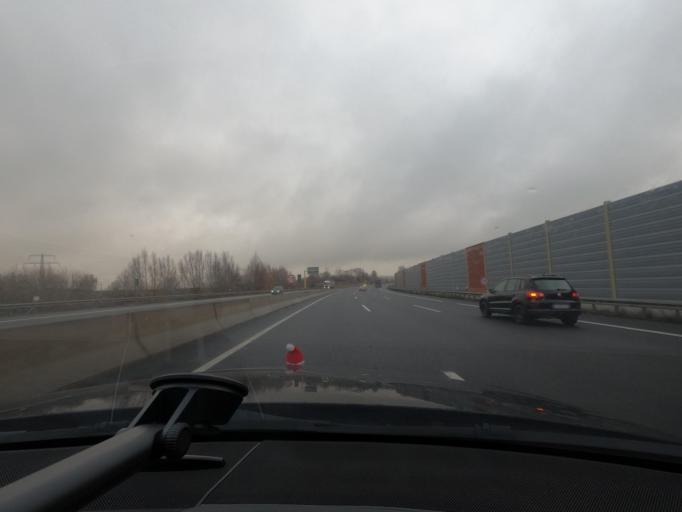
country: DE
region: Lower Saxony
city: Bovenden
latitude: 51.5647
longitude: 9.8813
